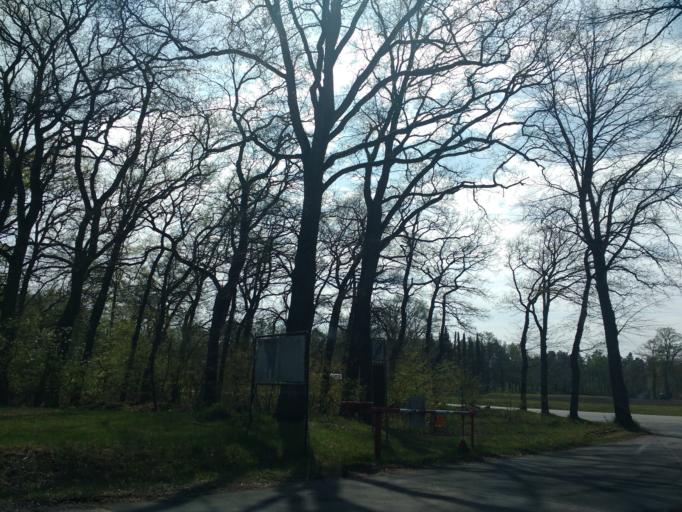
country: DE
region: North Rhine-Westphalia
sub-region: Regierungsbezirk Detmold
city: Hovelhof
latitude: 51.8233
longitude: 8.7200
